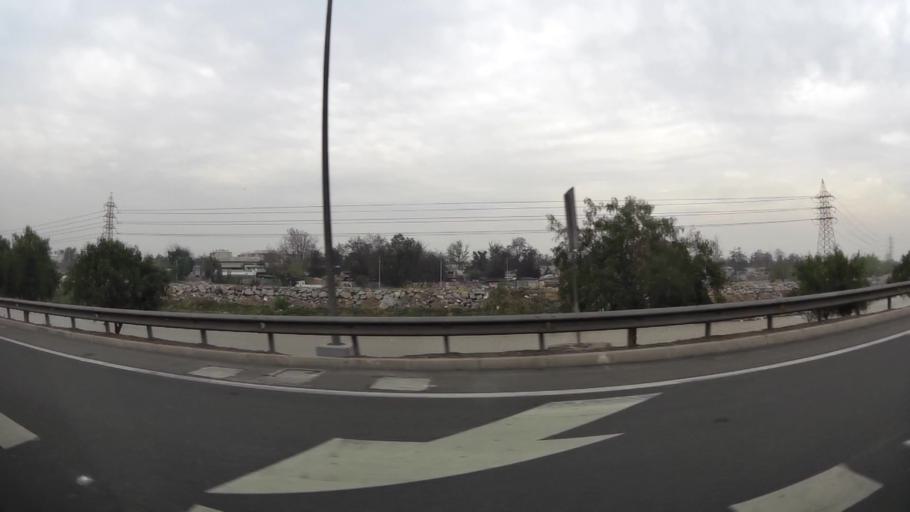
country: CL
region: Santiago Metropolitan
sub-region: Provincia de Santiago
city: Lo Prado
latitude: -33.4084
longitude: -70.7025
